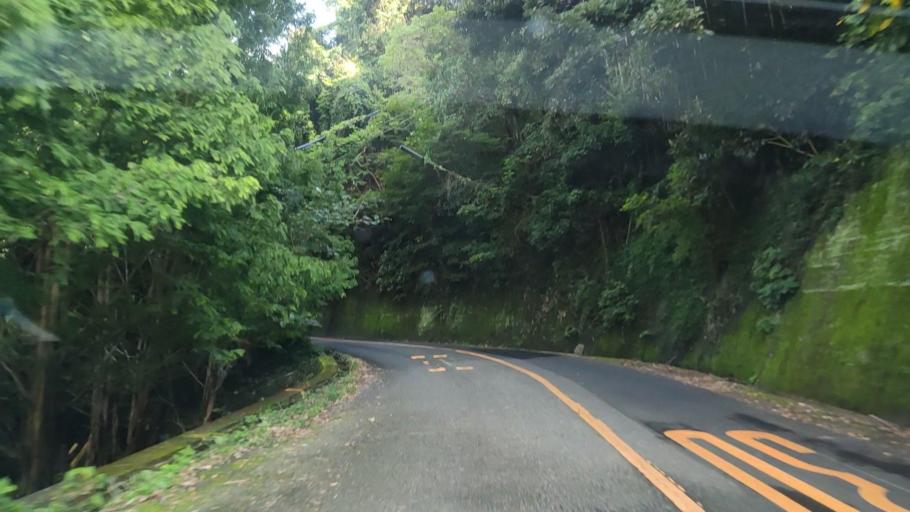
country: JP
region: Shizuoka
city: Shizuoka-shi
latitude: 34.9835
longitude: 138.4769
